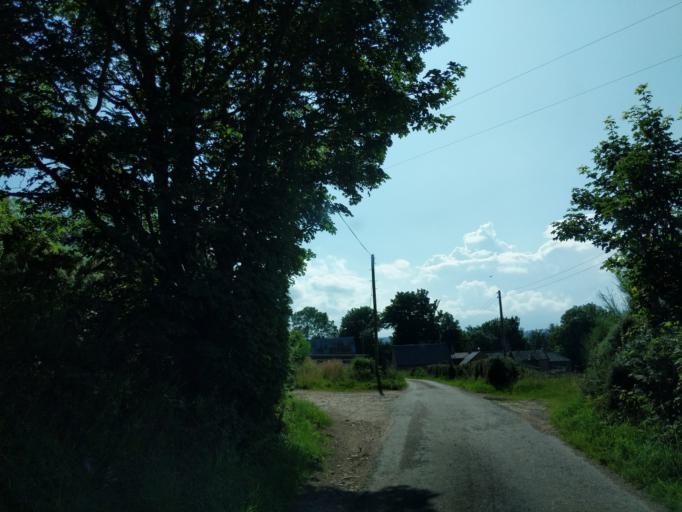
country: GB
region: Scotland
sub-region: Moray
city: Fochabers
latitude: 57.5991
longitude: -3.1077
